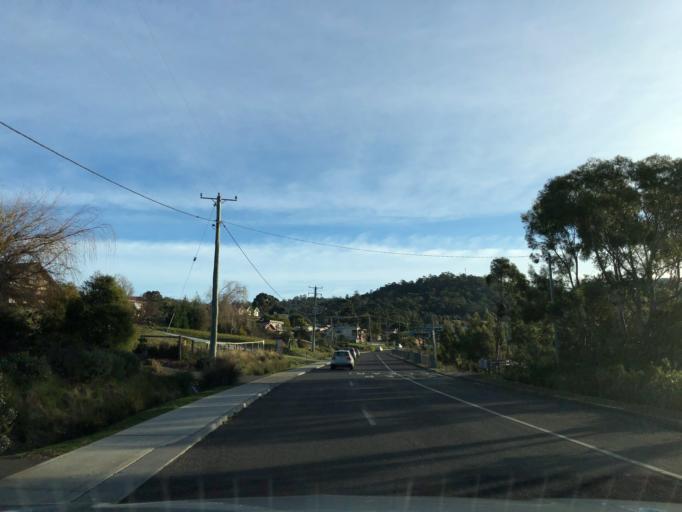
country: AU
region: Tasmania
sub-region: Kingborough
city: Kettering
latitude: -43.1284
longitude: 147.2512
